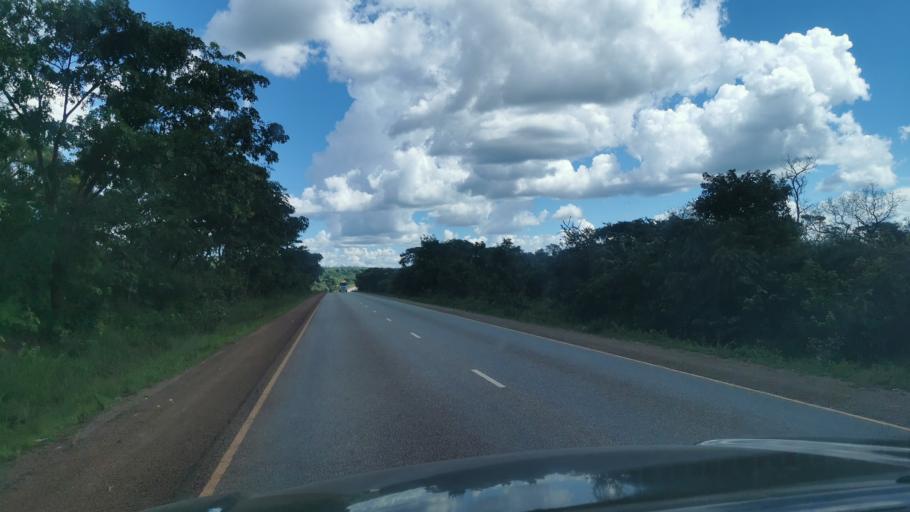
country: TZ
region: Geita
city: Uyovu
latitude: -3.0971
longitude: 31.3022
